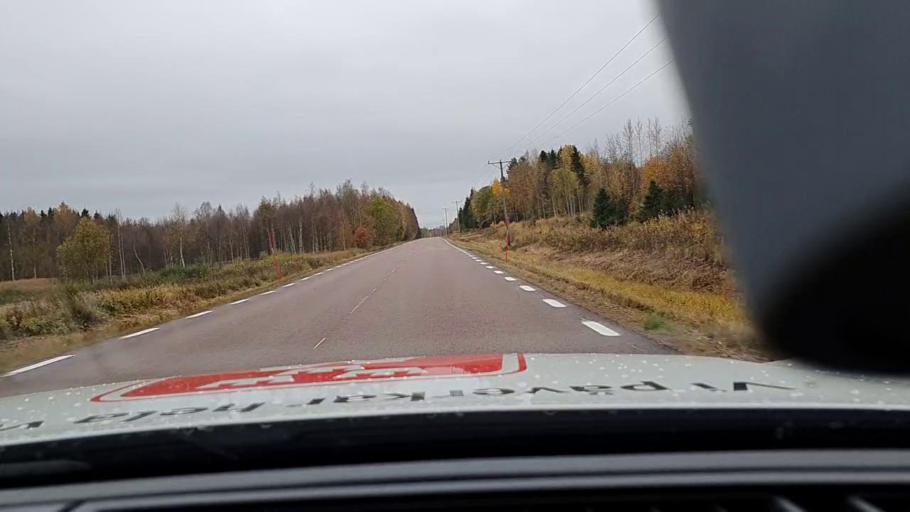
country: FI
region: Lapland
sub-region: Torniolaakso
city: Ylitornio
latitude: 66.1267
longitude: 23.9114
